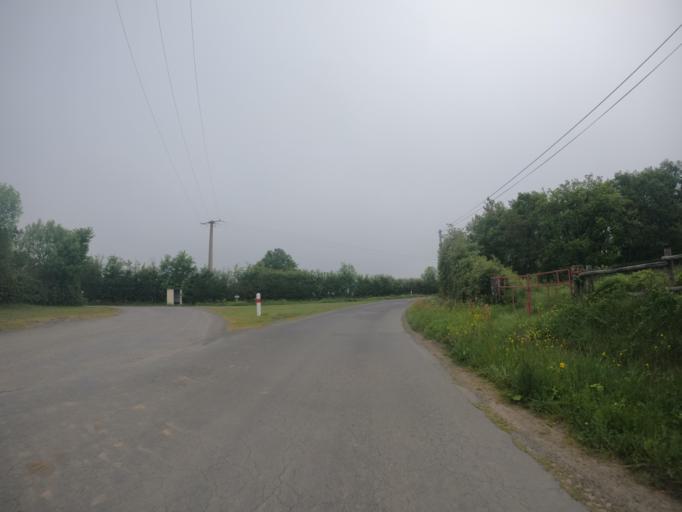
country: FR
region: Poitou-Charentes
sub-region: Departement des Deux-Sevres
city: Mauze-Thouarsais
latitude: 46.9004
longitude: -0.3413
